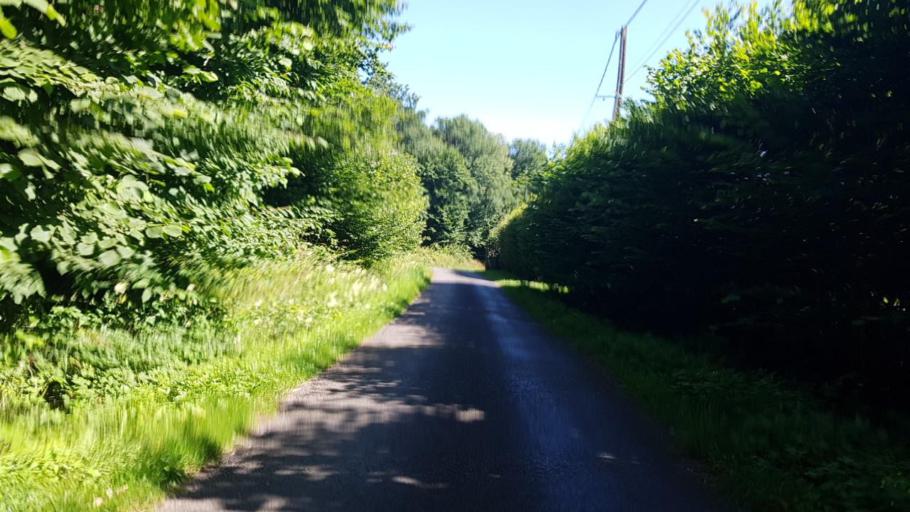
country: FR
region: Nord-Pas-de-Calais
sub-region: Departement du Nord
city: Anor
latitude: 50.0009
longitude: 4.1367
